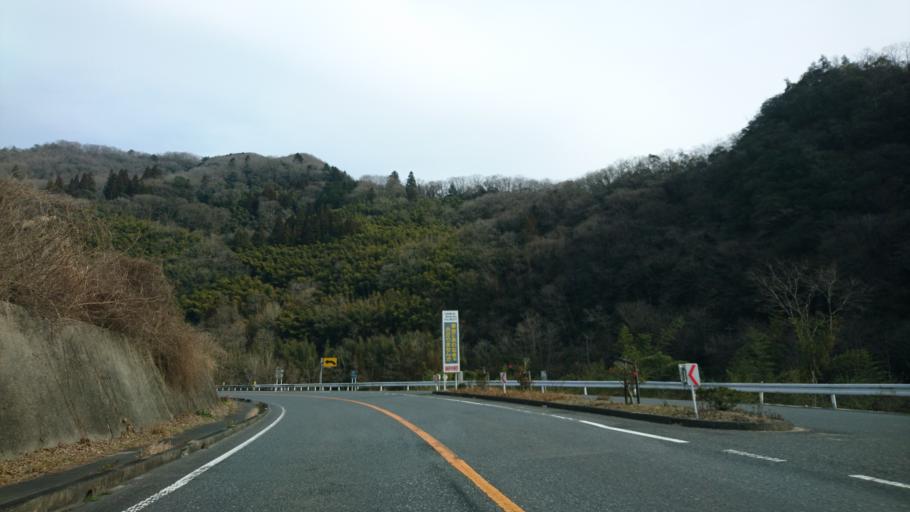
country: JP
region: Okayama
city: Takahashi
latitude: 34.8652
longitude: 133.5650
